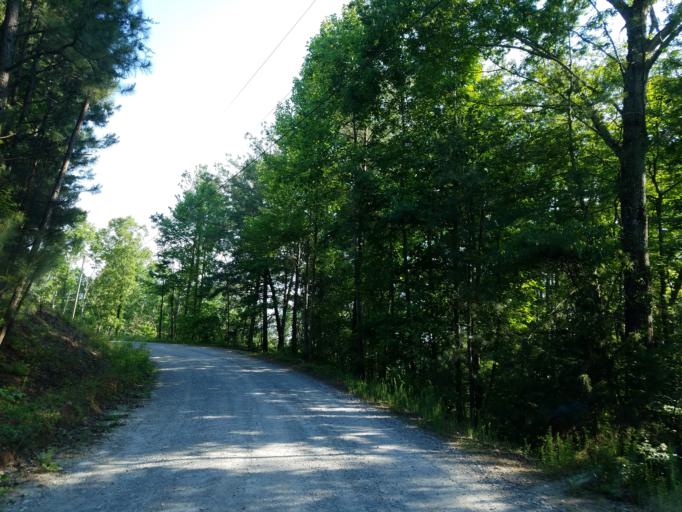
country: US
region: Georgia
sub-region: Pickens County
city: Nelson
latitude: 34.3717
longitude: -84.3413
